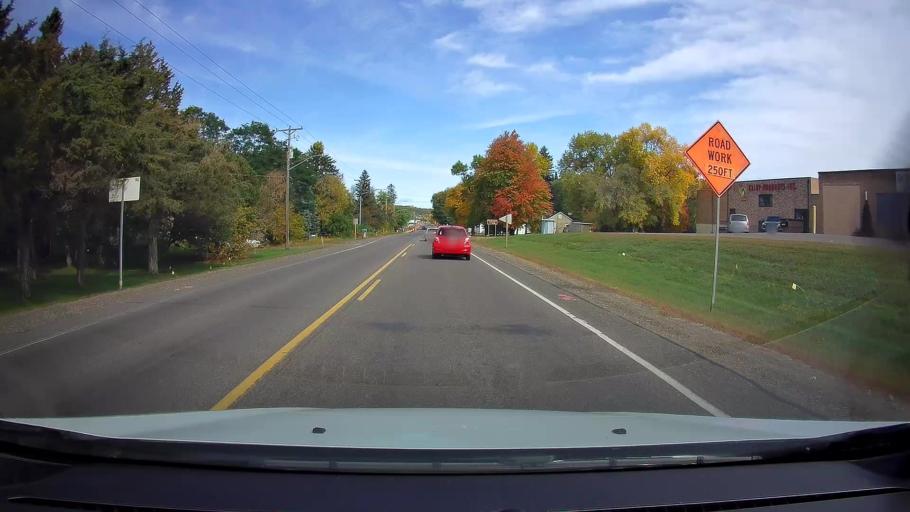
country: US
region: Wisconsin
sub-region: Polk County
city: Saint Croix Falls
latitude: 45.3523
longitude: -92.6377
